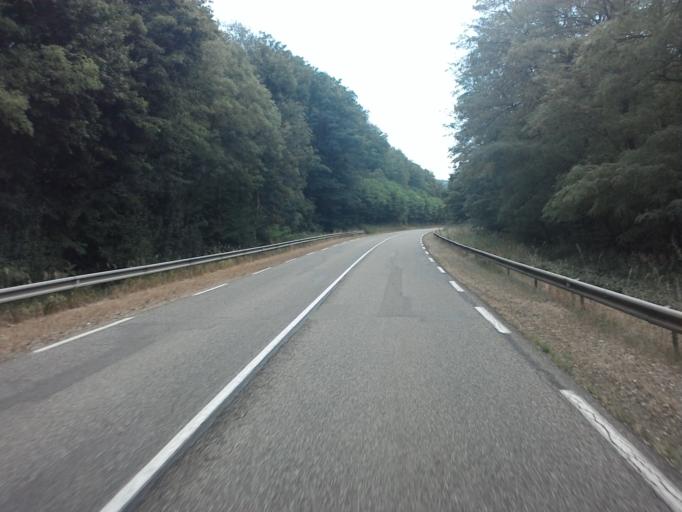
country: FR
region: Franche-Comte
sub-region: Departement du Jura
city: Saint-Amour
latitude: 46.4403
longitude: 5.3509
